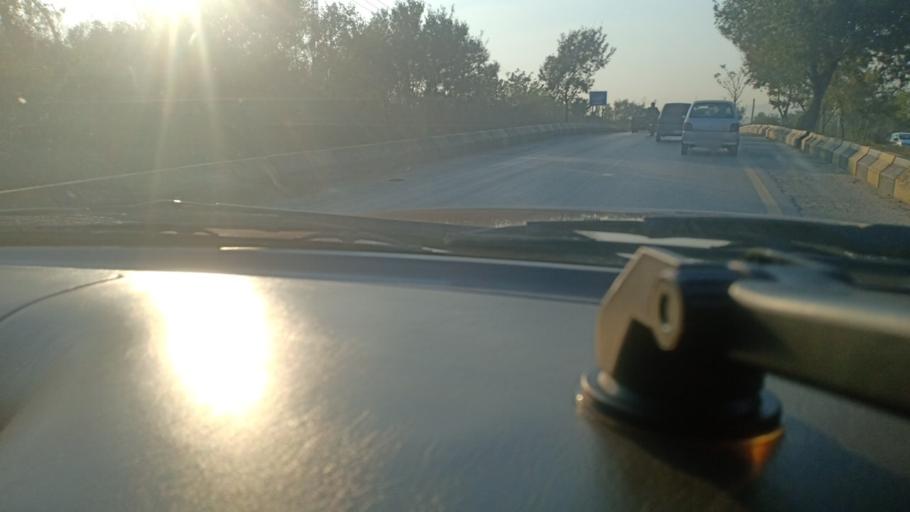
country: PK
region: Islamabad
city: Islamabad
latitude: 33.7348
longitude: 73.1621
